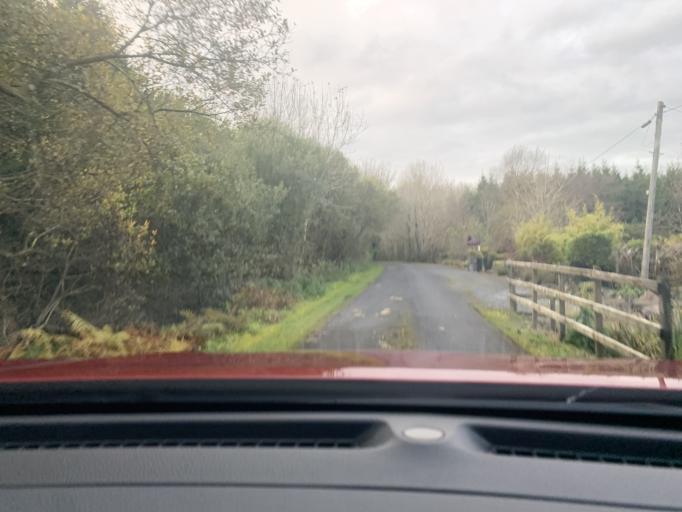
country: IE
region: Connaught
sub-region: Roscommon
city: Ballaghaderreen
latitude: 54.0131
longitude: -8.6117
